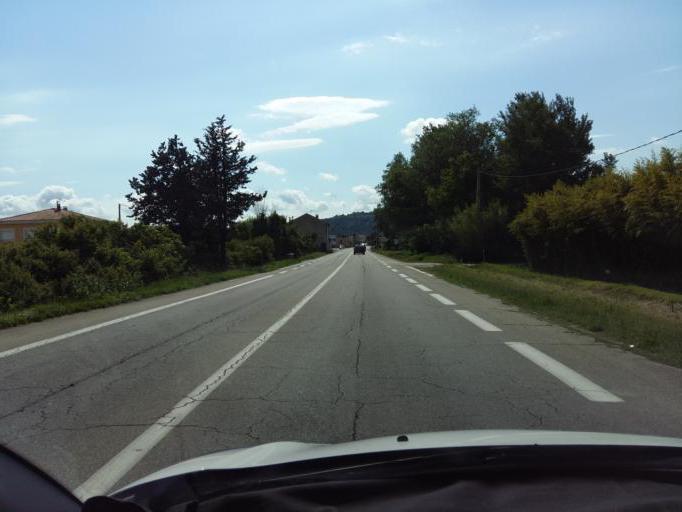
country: FR
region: Provence-Alpes-Cote d'Azur
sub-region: Departement du Vaucluse
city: Cavaillon
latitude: 43.8399
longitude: 5.0582
